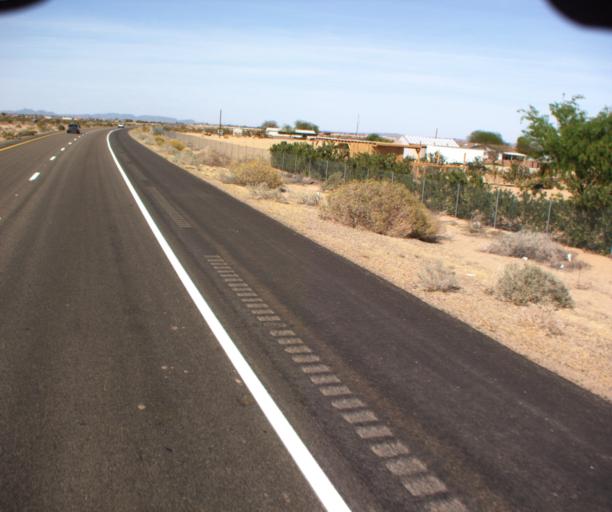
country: US
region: Arizona
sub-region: Yuma County
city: Fortuna Foothills
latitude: 32.6315
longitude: -114.5206
